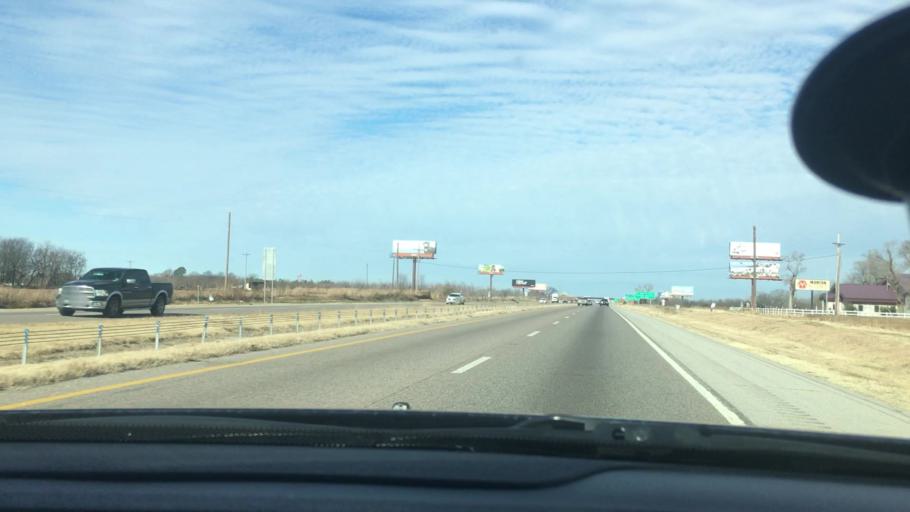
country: US
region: Oklahoma
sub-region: McClain County
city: Goldsby
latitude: 35.1449
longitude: -97.4690
